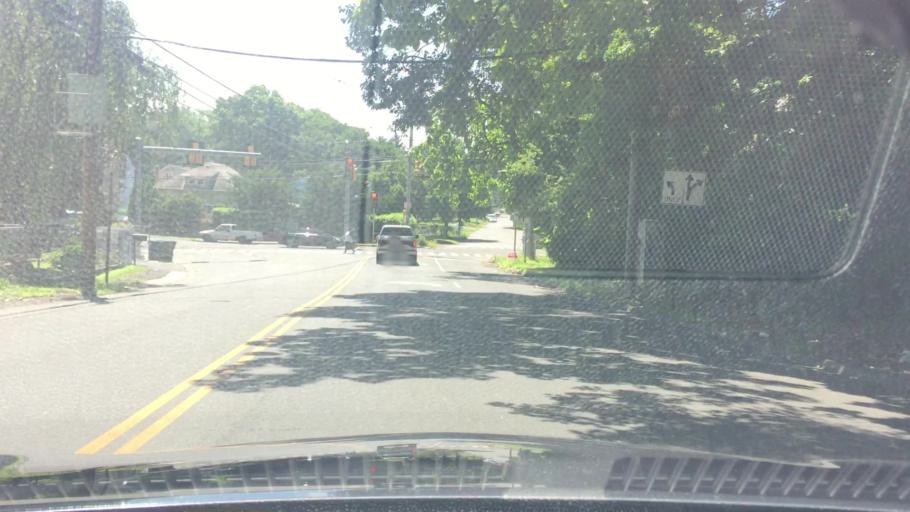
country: US
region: Connecticut
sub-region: Fairfield County
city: Trumbull
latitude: 41.2083
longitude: -73.1964
